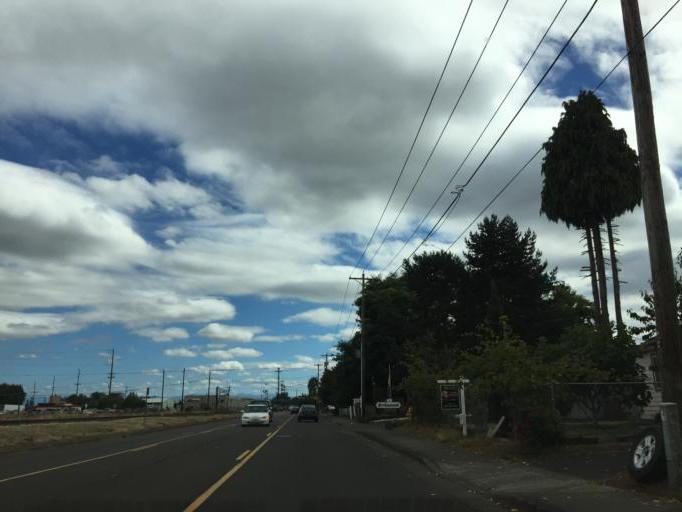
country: US
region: Oregon
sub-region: Marion County
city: Woodburn
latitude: 45.1365
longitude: -122.8473
